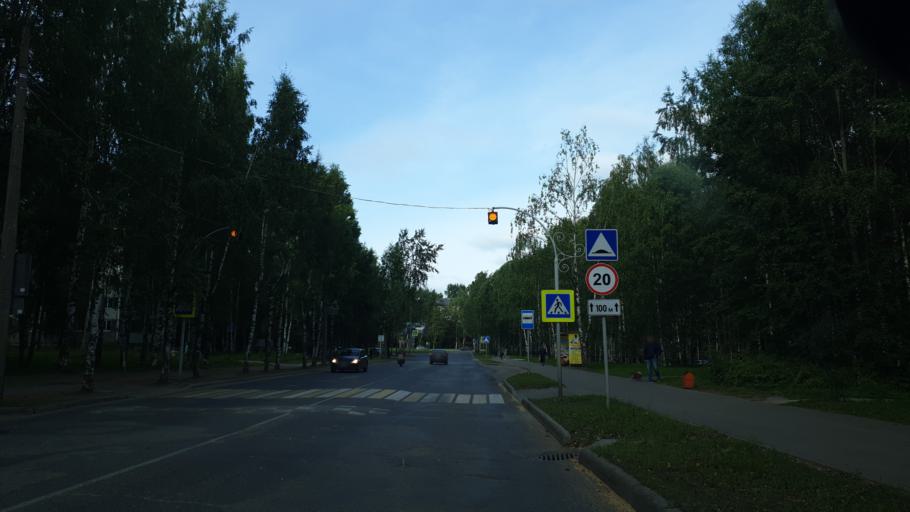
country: RU
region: Komi Republic
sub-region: Syktyvdinskiy Rayon
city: Syktyvkar
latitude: 61.6596
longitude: 50.8158
